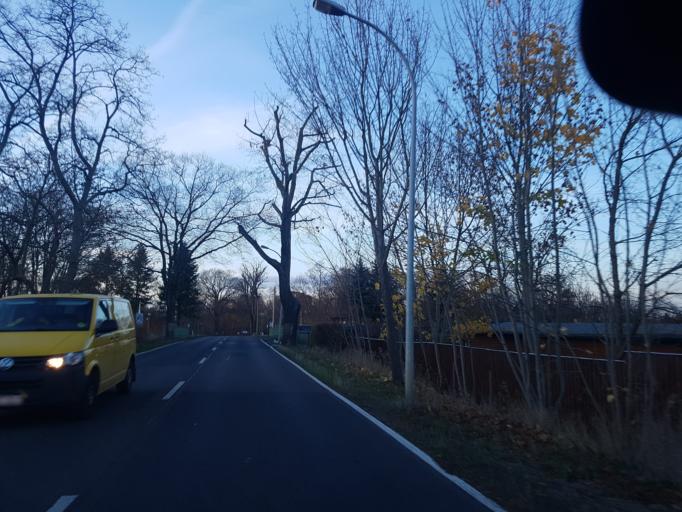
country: DE
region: Brandenburg
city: Finsterwalde
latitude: 51.6447
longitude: 13.6941
